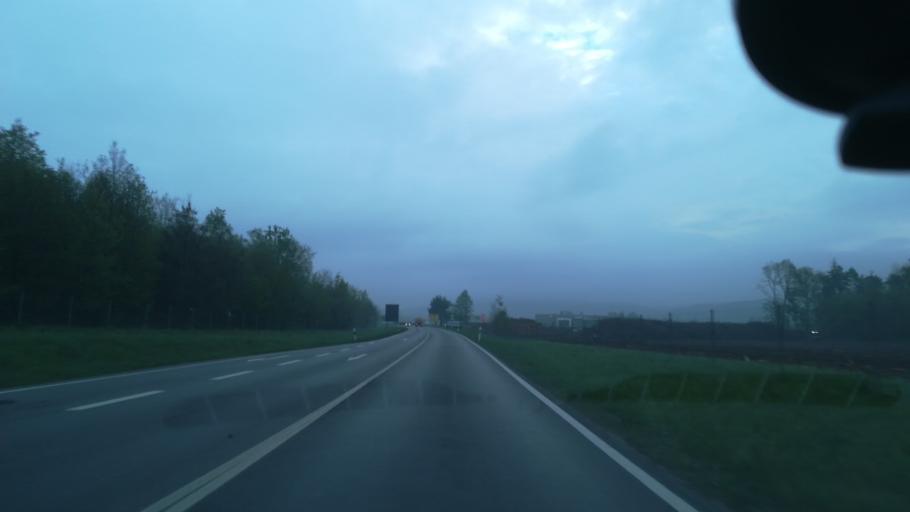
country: DE
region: Baden-Wuerttemberg
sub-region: Freiburg Region
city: Steisslingen
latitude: 47.7724
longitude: 8.9152
